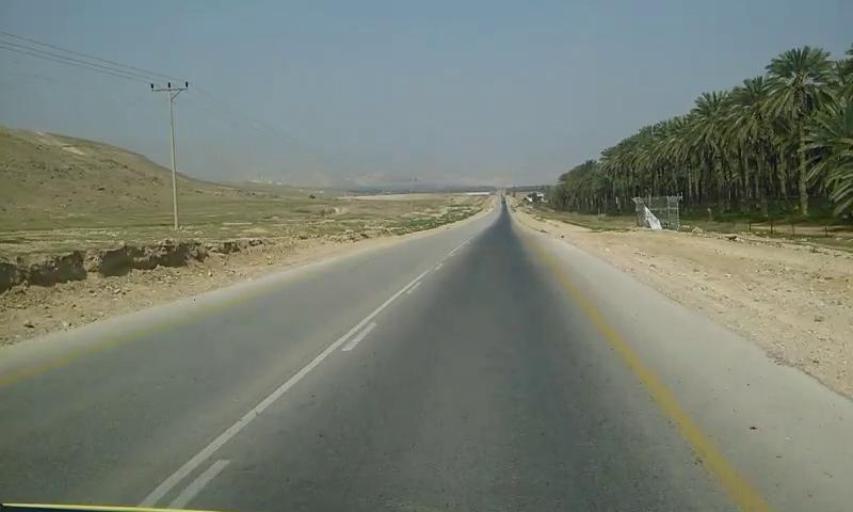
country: PS
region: West Bank
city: Al `Awja
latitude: 31.9786
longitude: 35.4668
